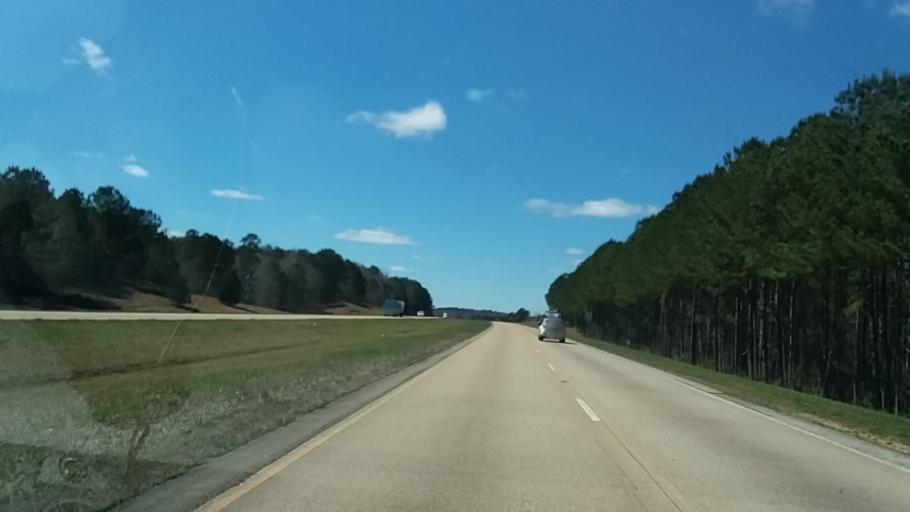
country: US
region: Mississippi
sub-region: Tishomingo County
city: Iuka
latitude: 34.8076
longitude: -88.2648
